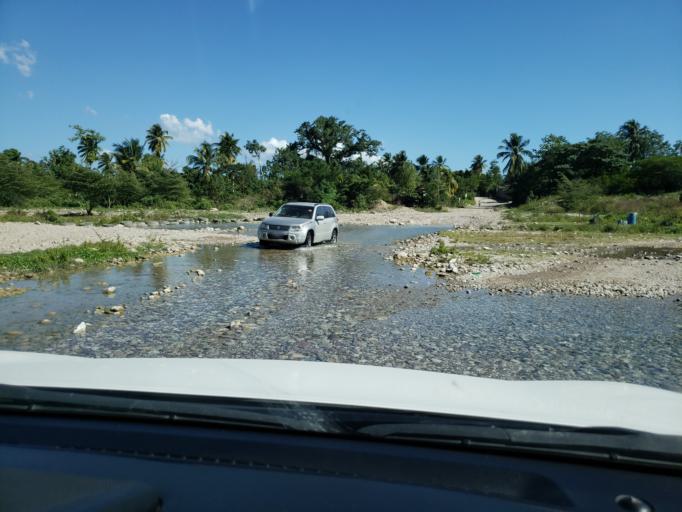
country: HT
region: Sud
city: Aquin
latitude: 18.3776
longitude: -73.4104
